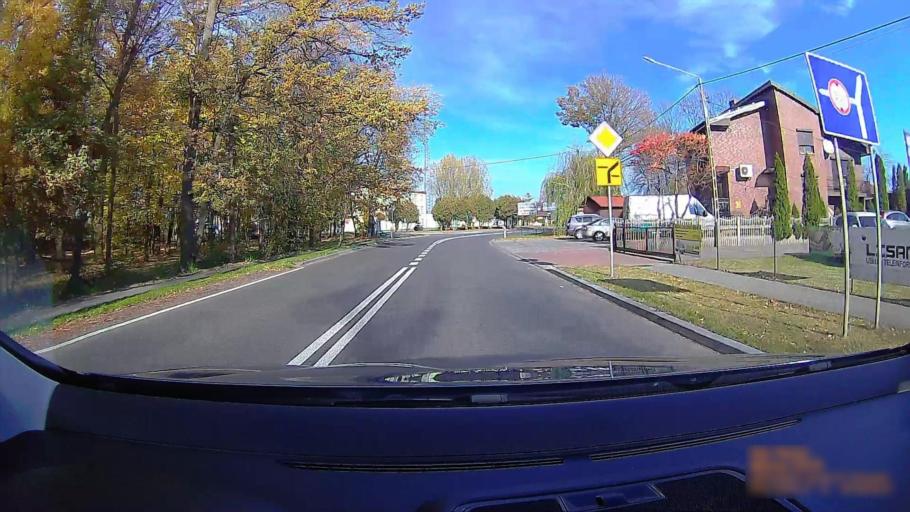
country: PL
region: Greater Poland Voivodeship
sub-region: Powiat ostrzeszowski
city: Doruchow
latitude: 51.4158
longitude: 18.0760
